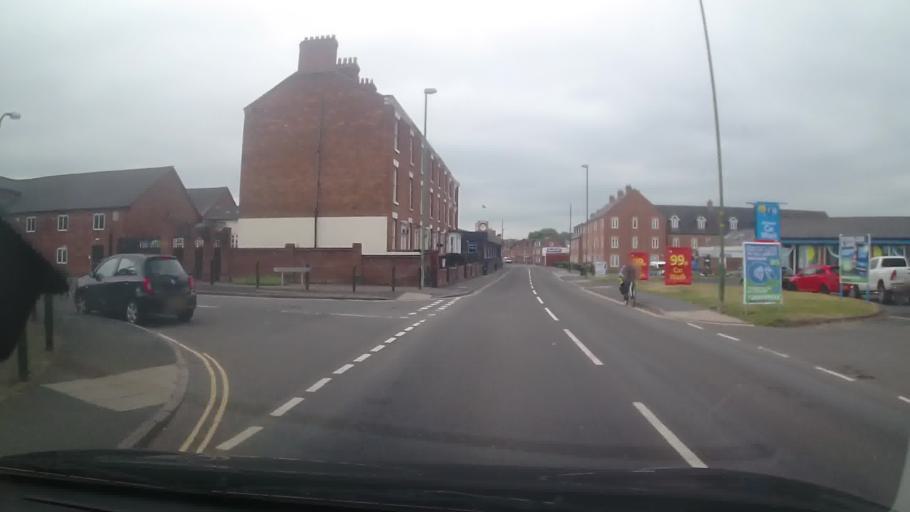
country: GB
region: England
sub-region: Shropshire
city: Shrewsbury
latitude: 52.7155
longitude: -2.7476
